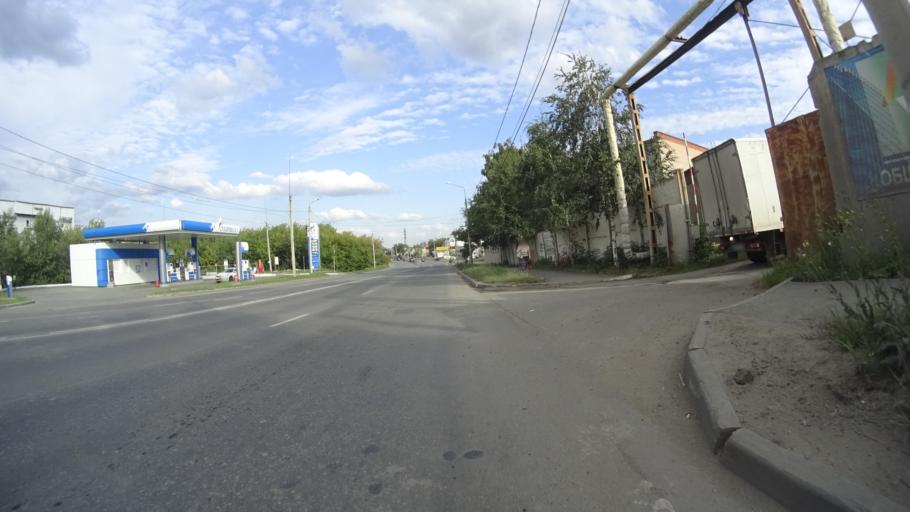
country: RU
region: Chelyabinsk
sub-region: Gorod Chelyabinsk
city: Chelyabinsk
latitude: 55.1980
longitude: 61.3674
